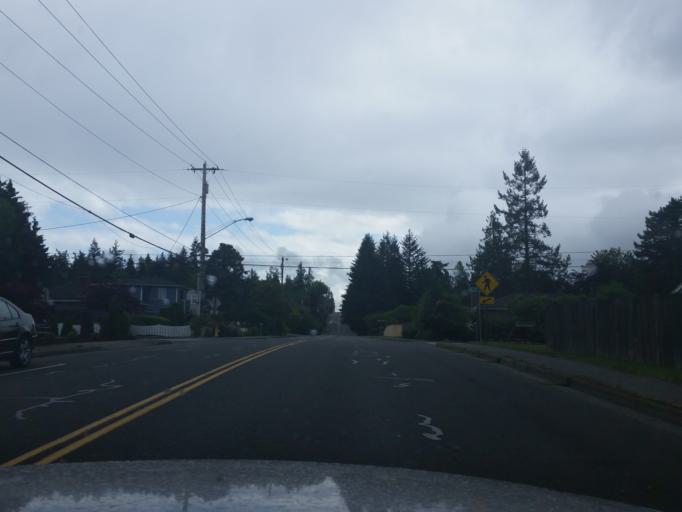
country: US
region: Washington
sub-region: Snohomish County
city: Edmonds
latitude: 47.8142
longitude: -122.3670
